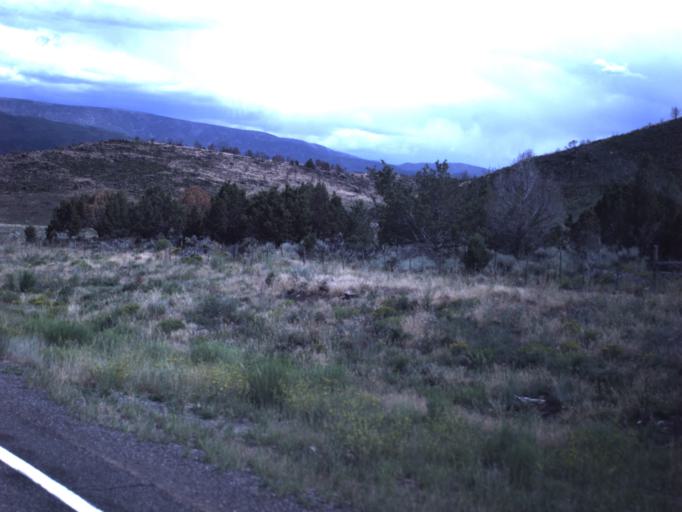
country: US
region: Utah
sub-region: Sevier County
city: Richfield
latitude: 38.6892
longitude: -111.8658
